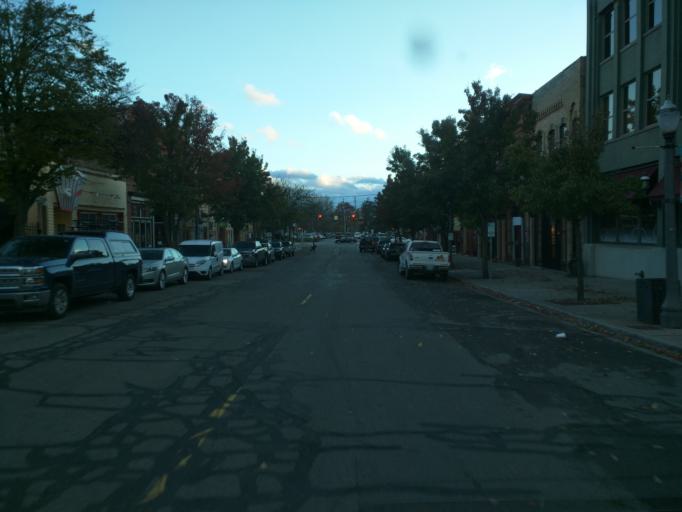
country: US
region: Michigan
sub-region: Ingham County
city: Lansing
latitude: 42.7484
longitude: -84.5496
